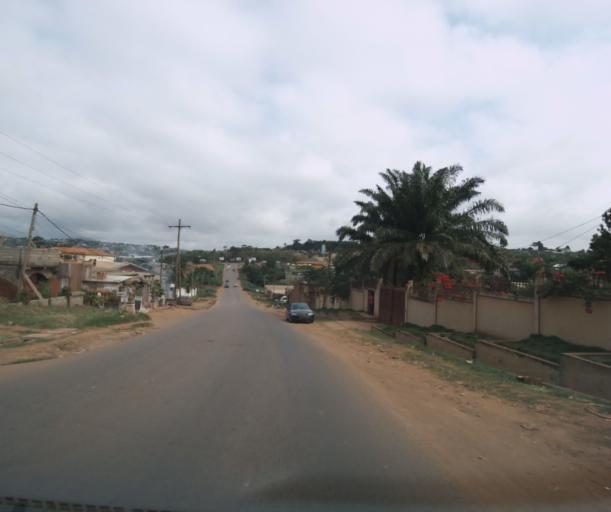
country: CM
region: Centre
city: Yaounde
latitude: 3.8056
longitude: 11.5212
